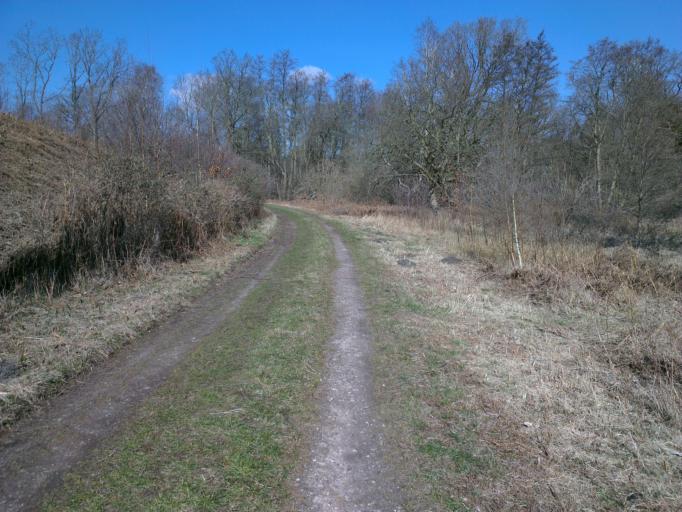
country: DK
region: Capital Region
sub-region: Frederikssund Kommune
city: Jaegerspris
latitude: 55.9276
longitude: 11.9411
